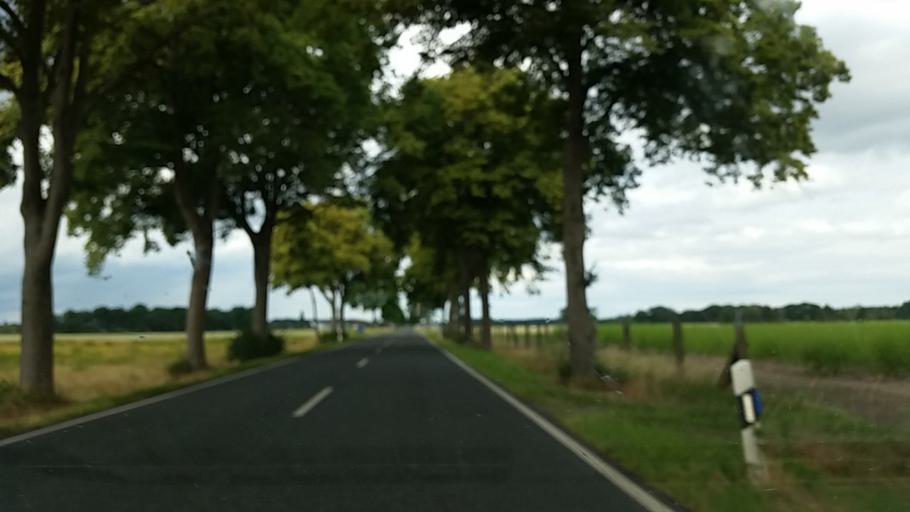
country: DE
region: Lower Saxony
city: Ribbesbuttel
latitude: 52.4395
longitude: 10.5310
